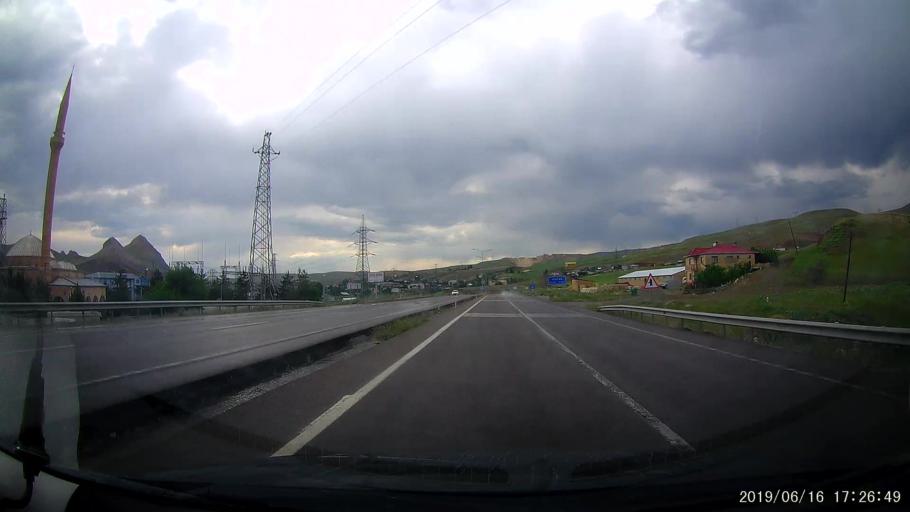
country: TR
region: Erzincan
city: Tercan
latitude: 39.7721
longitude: 40.4047
